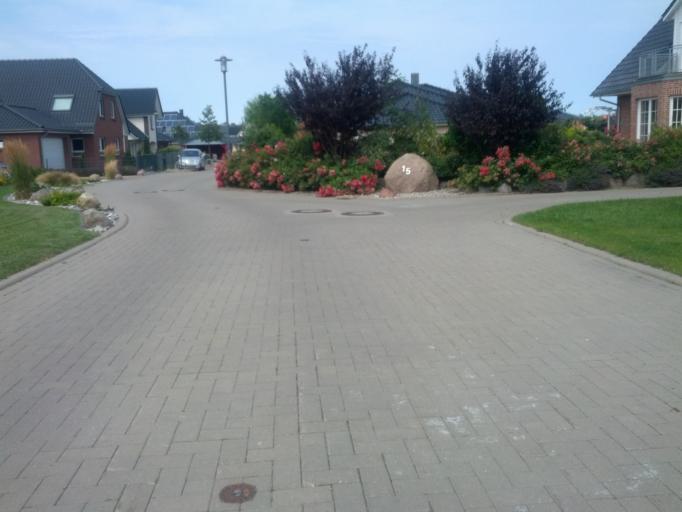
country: DE
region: Mecklenburg-Vorpommern
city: Bastorf
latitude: 54.1424
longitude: 11.7201
